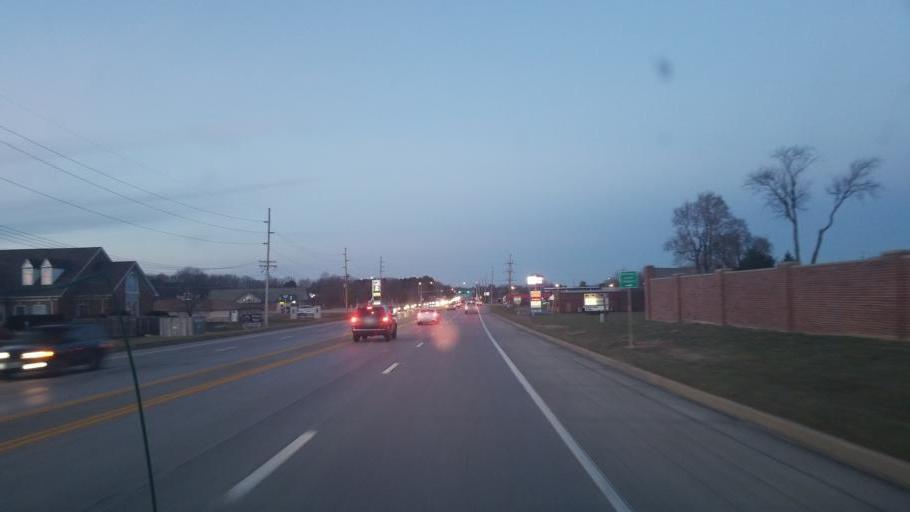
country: US
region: Missouri
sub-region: Howell County
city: West Plains
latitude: 36.7292
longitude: -91.8773
